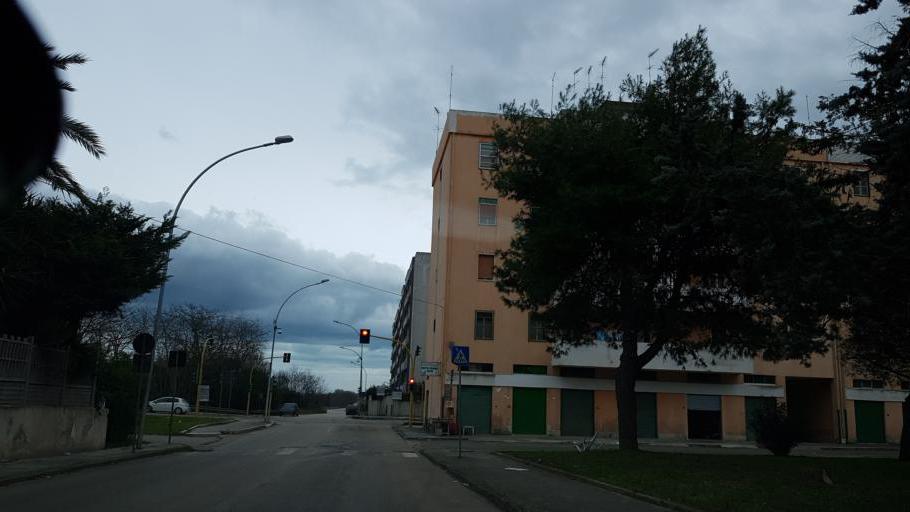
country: IT
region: Apulia
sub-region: Provincia di Brindisi
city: Brindisi
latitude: 40.6198
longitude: 17.9326
